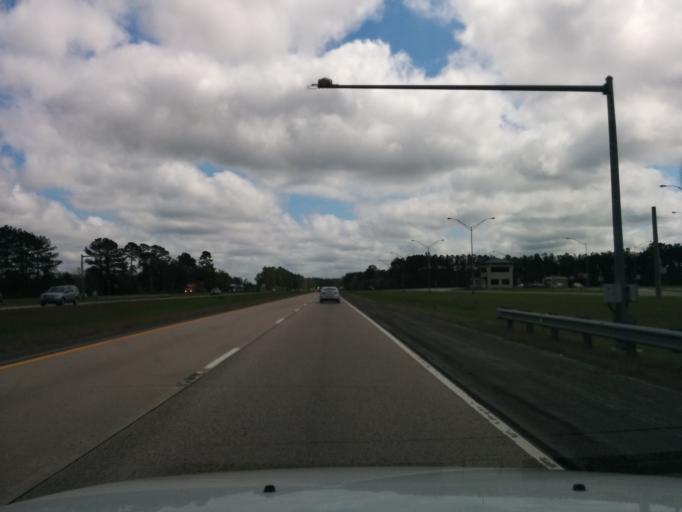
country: US
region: Georgia
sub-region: Chatham County
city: Bloomingdale
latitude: 32.1690
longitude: -81.4444
